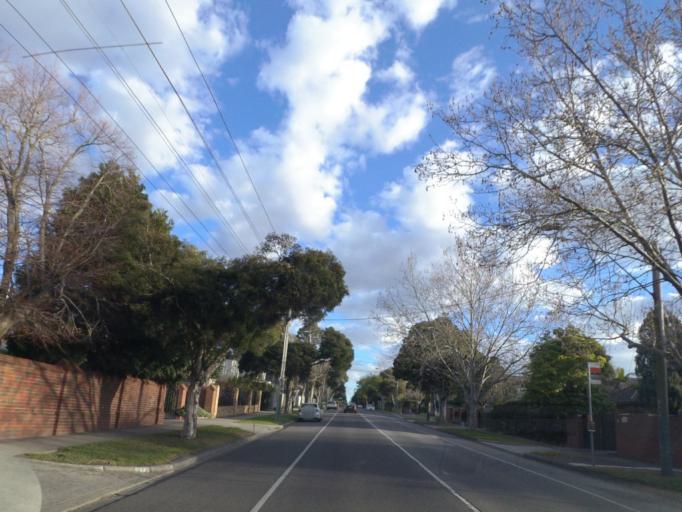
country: AU
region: Victoria
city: Mont Albert
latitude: -37.8082
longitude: 145.1008
